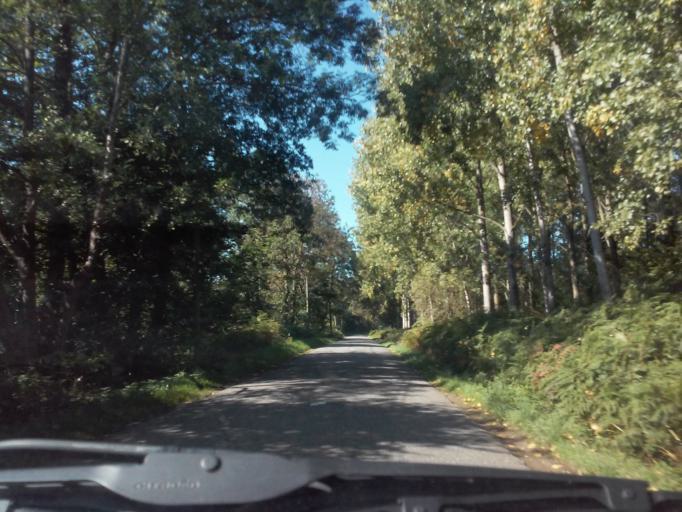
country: FR
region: Brittany
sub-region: Departement d'Ille-et-Vilaine
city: Saint-Medard-sur-Ille
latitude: 48.2398
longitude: -1.6487
